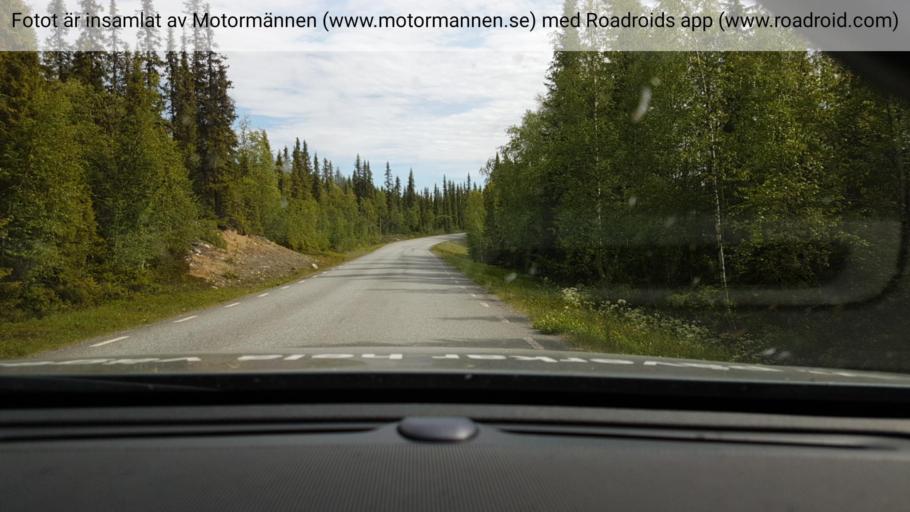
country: SE
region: Vaesterbotten
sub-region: Vilhelmina Kommun
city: Sjoberg
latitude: 65.2250
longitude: 16.0208
